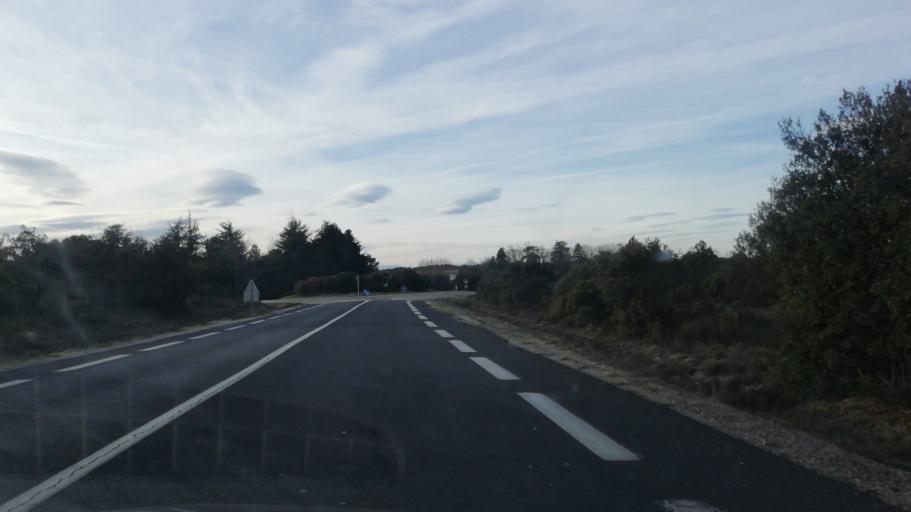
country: FR
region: Languedoc-Roussillon
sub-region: Departement du Gard
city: Clarensac
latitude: 43.8603
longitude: 4.2177
